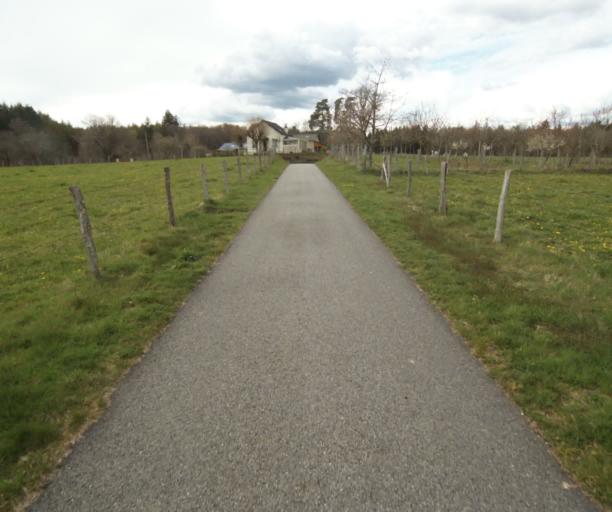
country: FR
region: Limousin
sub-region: Departement de la Correze
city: Argentat
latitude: 45.2161
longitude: 1.9601
